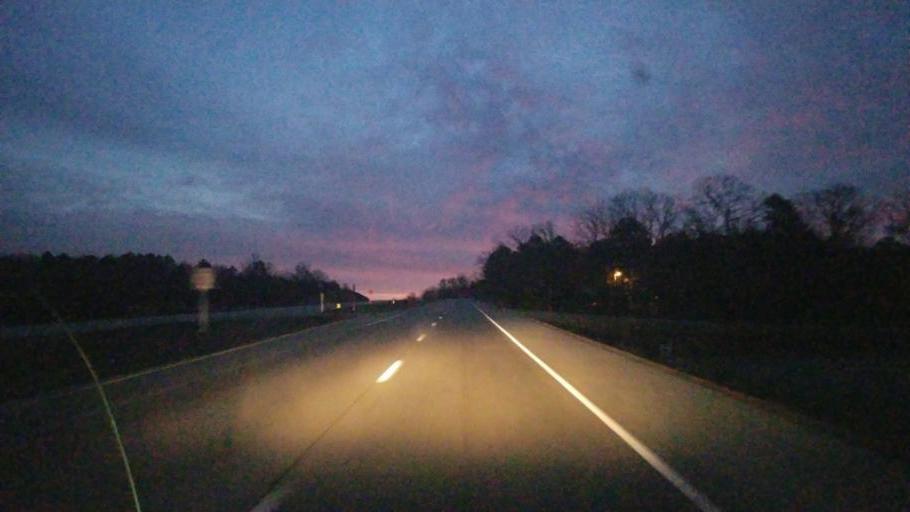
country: US
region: Missouri
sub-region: Howell County
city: Mountain View
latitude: 36.9906
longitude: -91.5255
